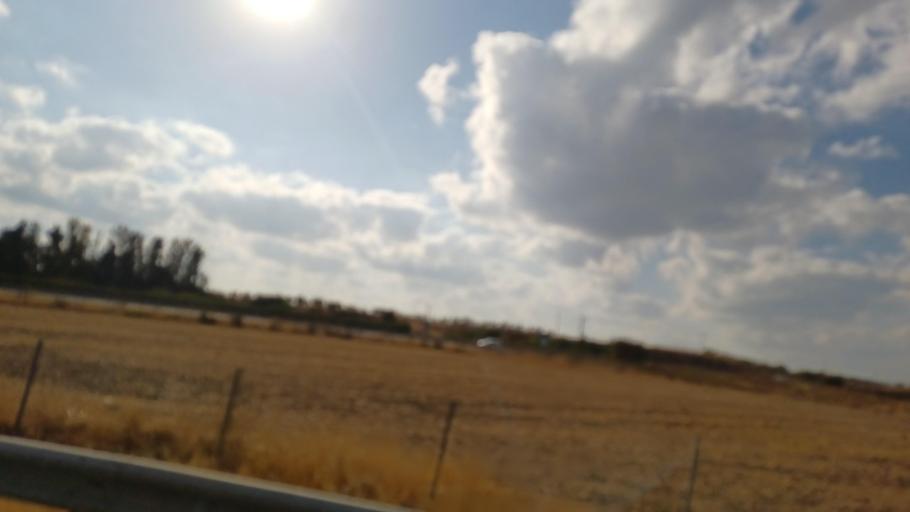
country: CY
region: Limassol
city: Pissouri
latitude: 34.7076
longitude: 32.5623
